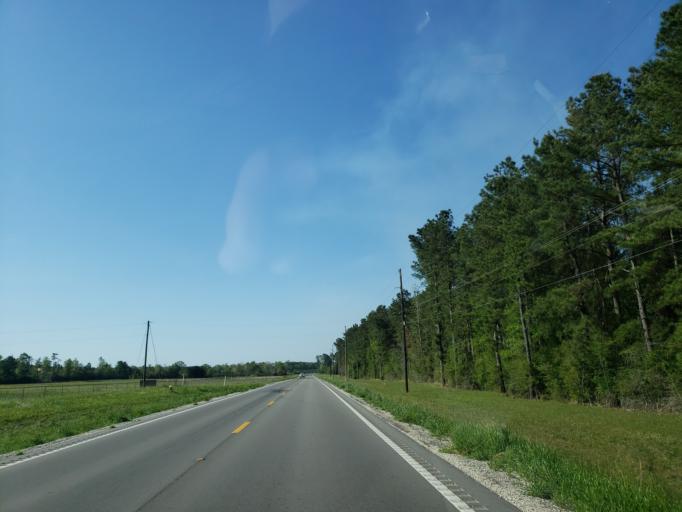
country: US
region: Mississippi
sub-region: Perry County
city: Richton
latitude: 31.3187
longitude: -88.9323
